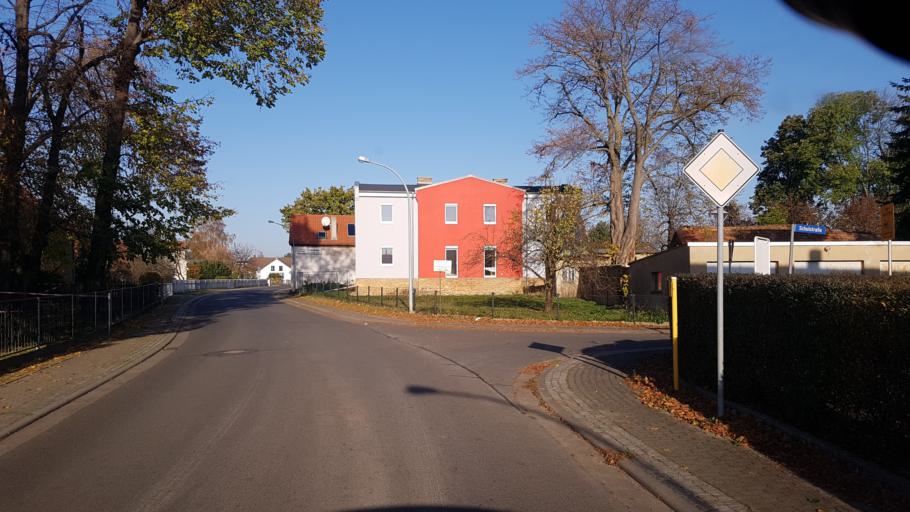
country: DE
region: Brandenburg
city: Schipkau
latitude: 51.5652
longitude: 13.9241
